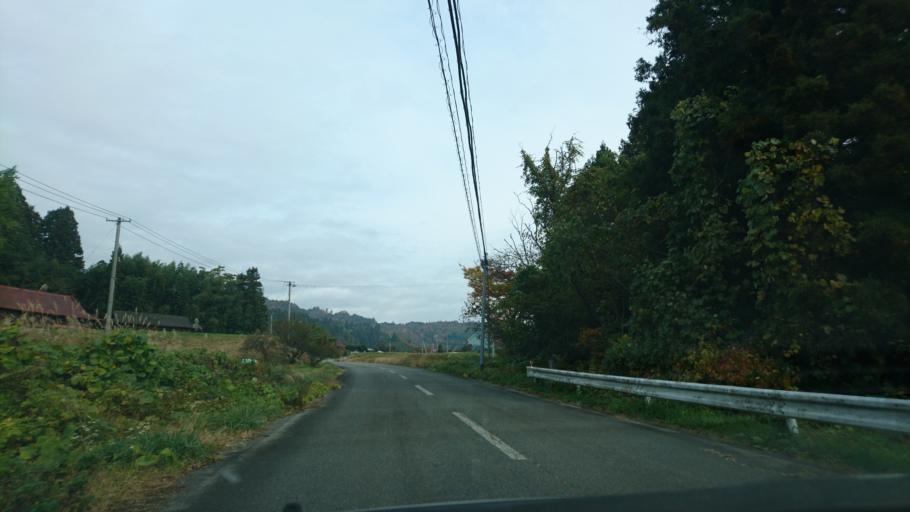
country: JP
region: Iwate
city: Ichinoseki
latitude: 38.9735
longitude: 141.1790
